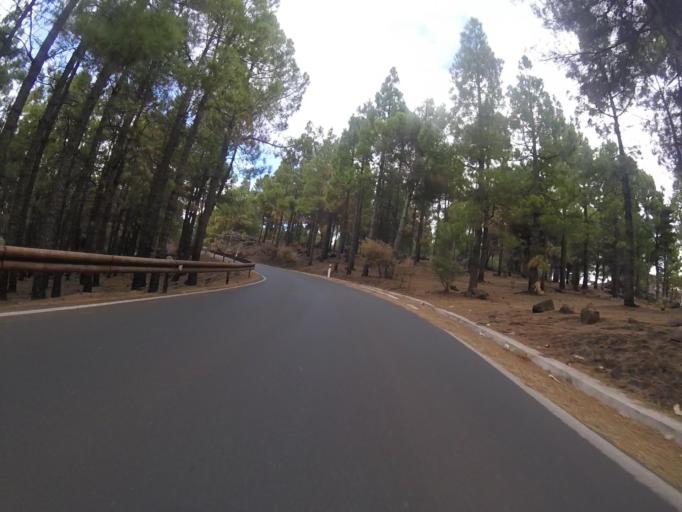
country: ES
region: Canary Islands
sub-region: Provincia de Las Palmas
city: Tejeda
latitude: 27.9731
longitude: -15.5739
